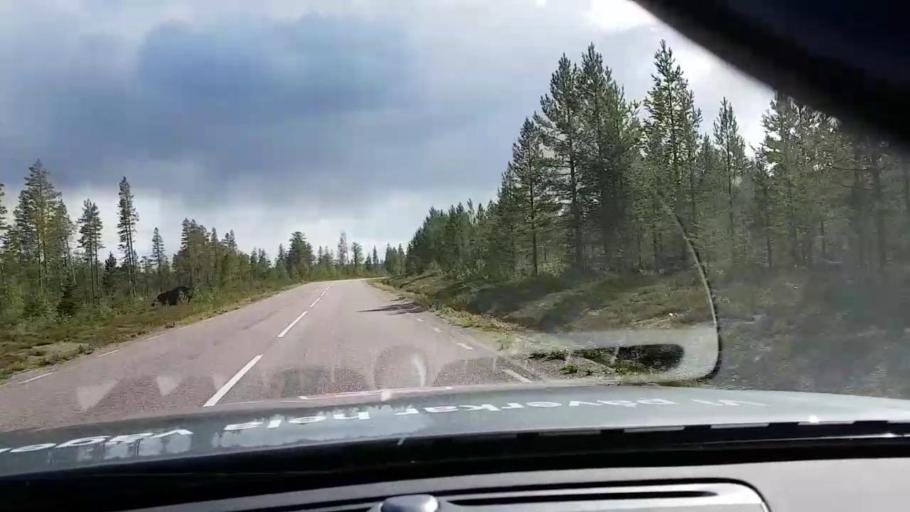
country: SE
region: Vaesterbotten
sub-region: Asele Kommun
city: Asele
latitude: 63.8975
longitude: 17.3496
